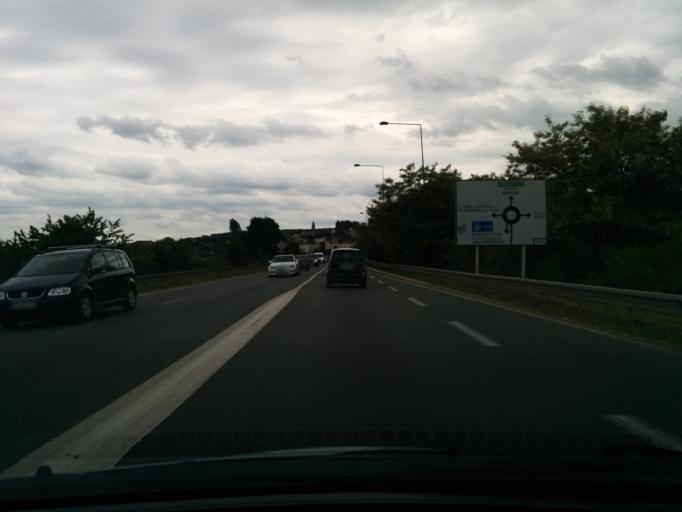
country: FR
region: Ile-de-France
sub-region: Departement des Yvelines
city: Epone
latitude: 48.9644
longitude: 1.8112
